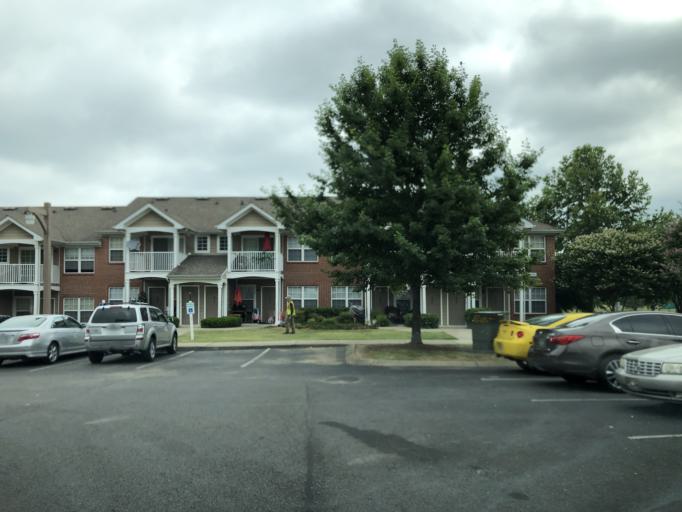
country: US
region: Tennessee
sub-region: Davidson County
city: Goodlettsville
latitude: 36.2959
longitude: -86.7277
